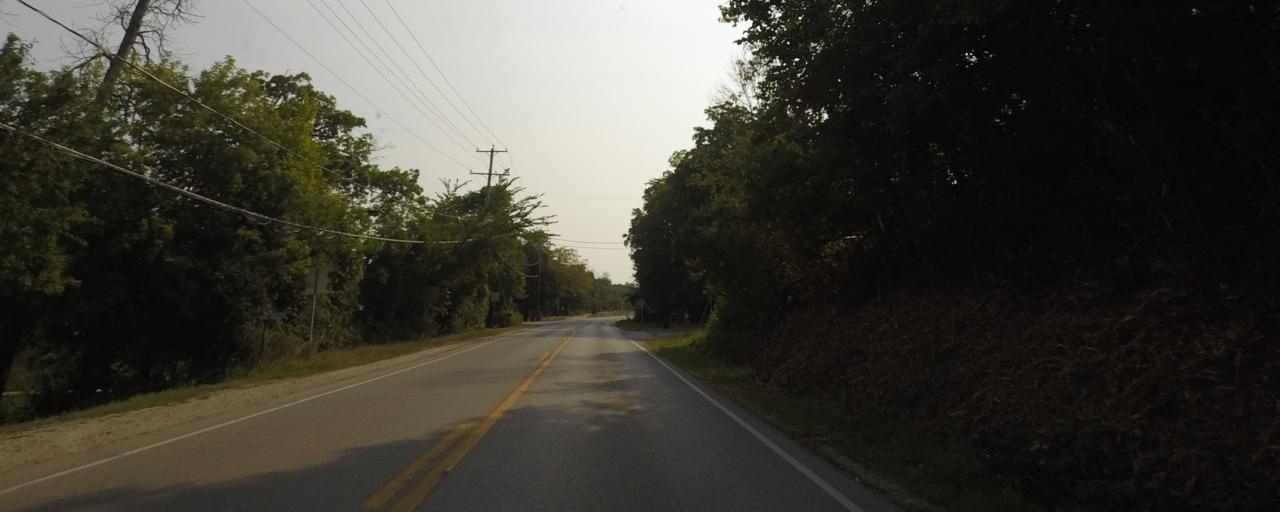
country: US
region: Wisconsin
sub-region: Waukesha County
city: Delafield
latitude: 43.0583
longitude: -88.4243
